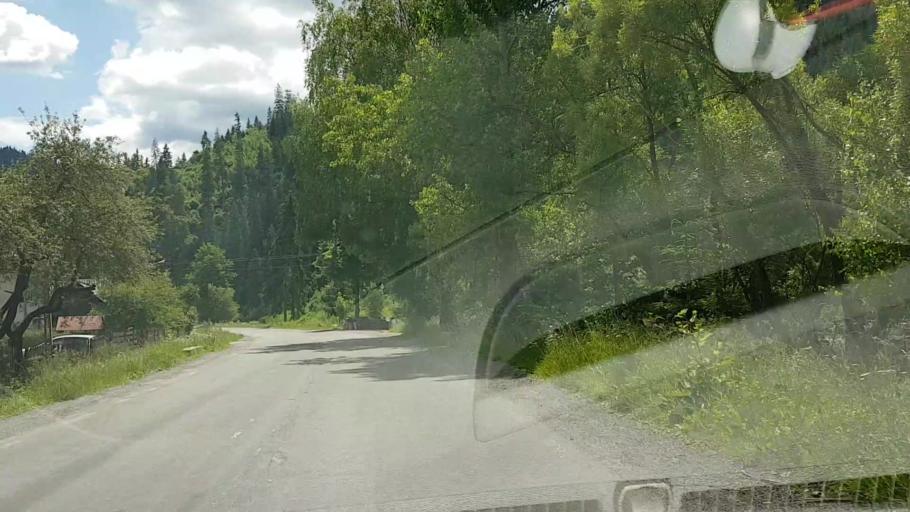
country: RO
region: Suceava
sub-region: Comuna Brosteni
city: Brosteni
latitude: 47.2405
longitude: 25.6911
